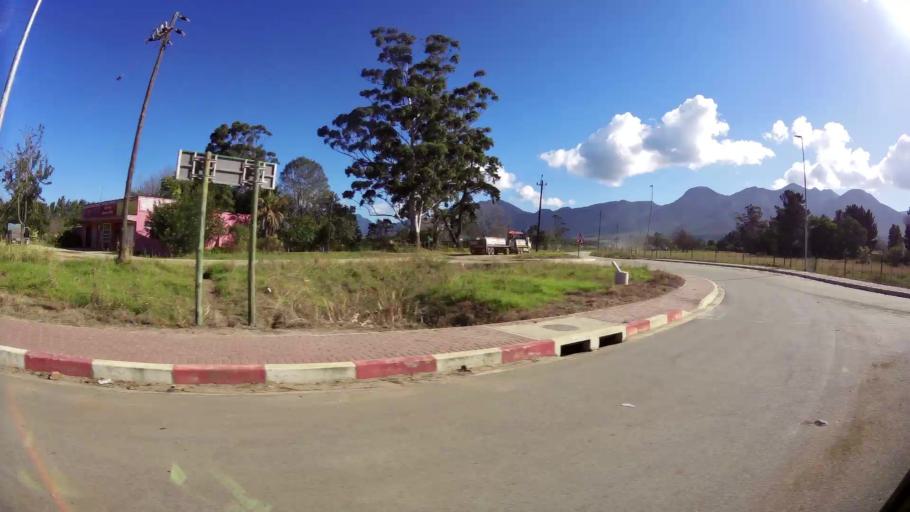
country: ZA
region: Western Cape
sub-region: Eden District Municipality
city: George
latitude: -33.9552
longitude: 22.3959
